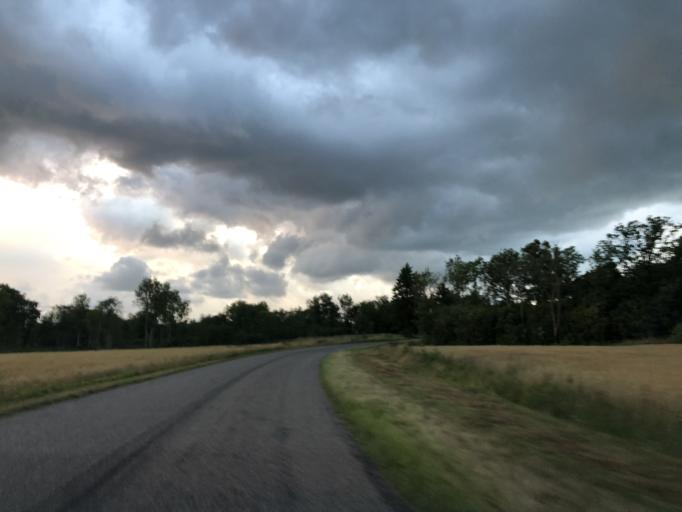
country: EE
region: Laeaene
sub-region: Ridala Parish
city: Uuemoisa
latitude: 58.8932
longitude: 23.6771
